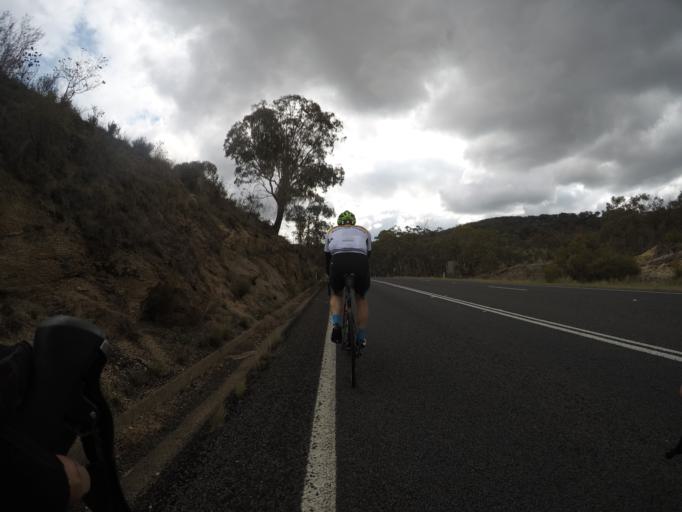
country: AU
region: New South Wales
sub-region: Bathurst Regional
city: Eglinton
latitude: -33.4215
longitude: 149.4166
